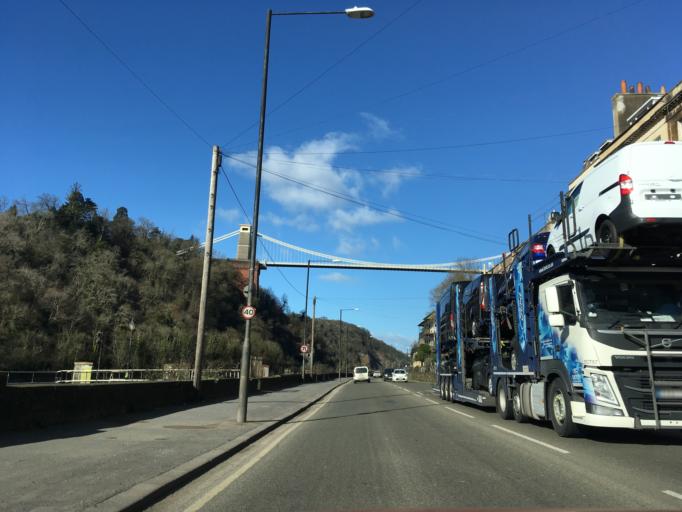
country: GB
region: England
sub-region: Bristol
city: Bristol
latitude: 51.4516
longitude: -2.6257
